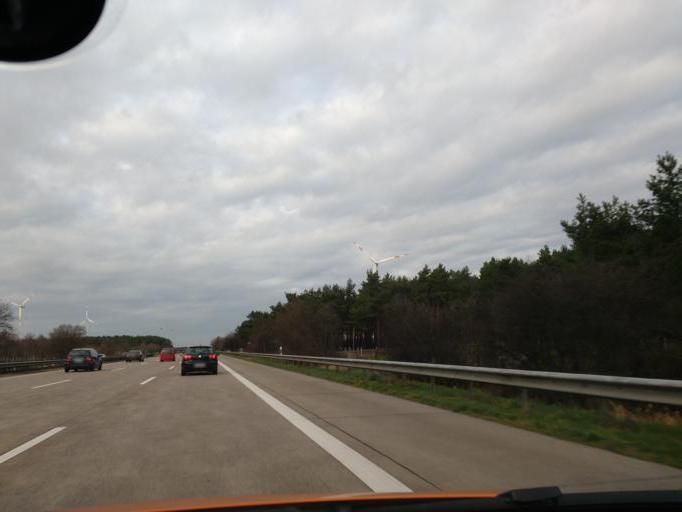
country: DE
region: Lower Saxony
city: Lindwedel
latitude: 52.6366
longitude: 9.7171
